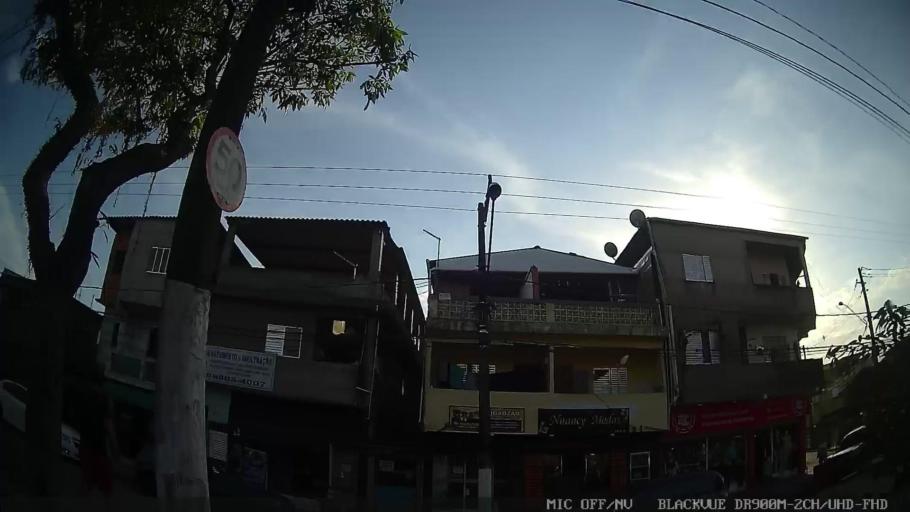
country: BR
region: Sao Paulo
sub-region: Cubatao
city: Cubatao
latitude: -23.9041
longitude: -46.4232
